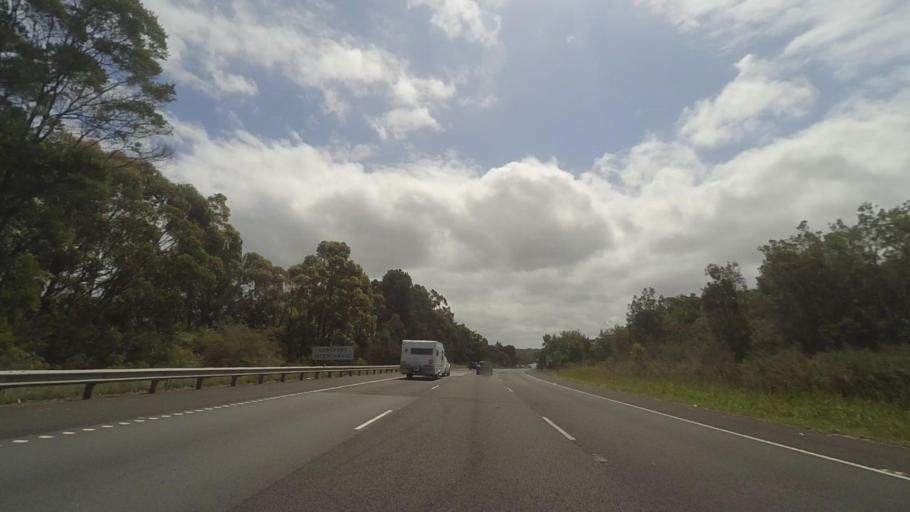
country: AU
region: New South Wales
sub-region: Gosford Shire
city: Narara
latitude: -33.3675
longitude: 151.3286
